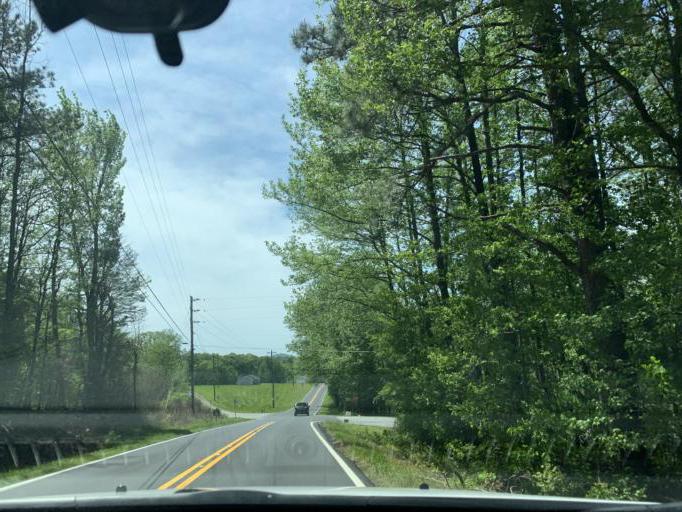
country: US
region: Georgia
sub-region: Forsyth County
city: Cumming
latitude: 34.2645
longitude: -84.0471
